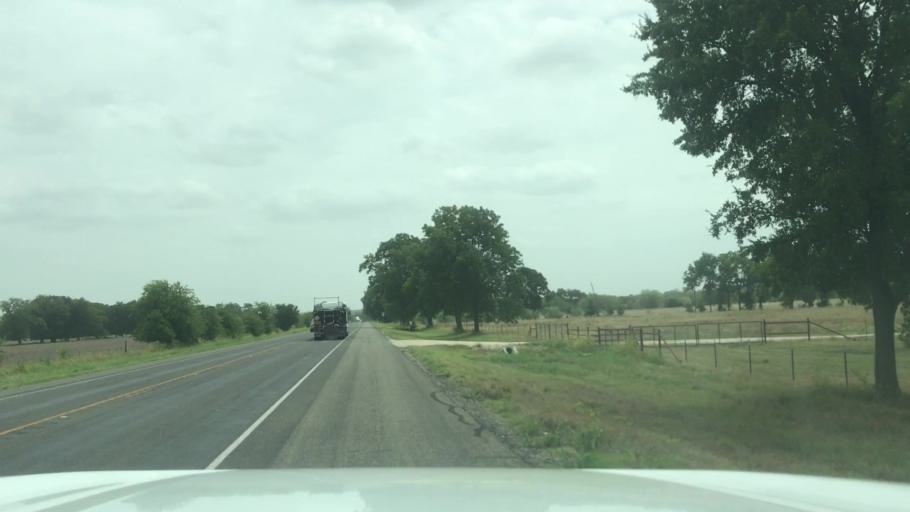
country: US
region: Texas
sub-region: Bosque County
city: Valley Mills
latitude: 31.6732
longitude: -97.5071
